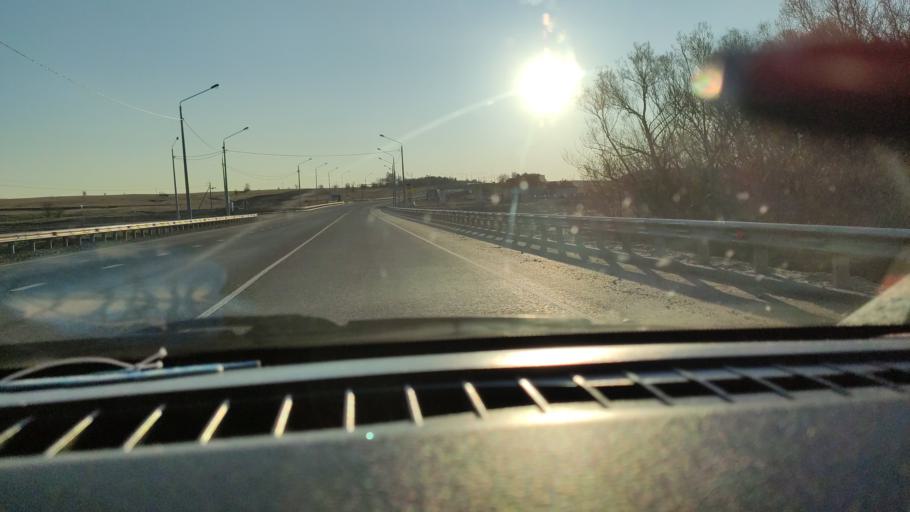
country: RU
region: Saratov
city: Sennoy
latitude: 52.1594
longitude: 47.0805
